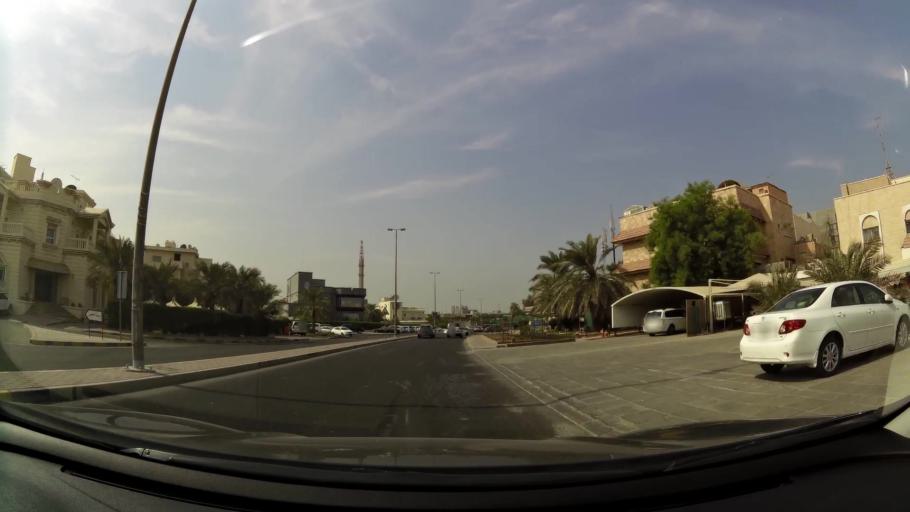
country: KW
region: Al Asimah
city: Ash Shamiyah
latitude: 29.3382
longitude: 47.9552
